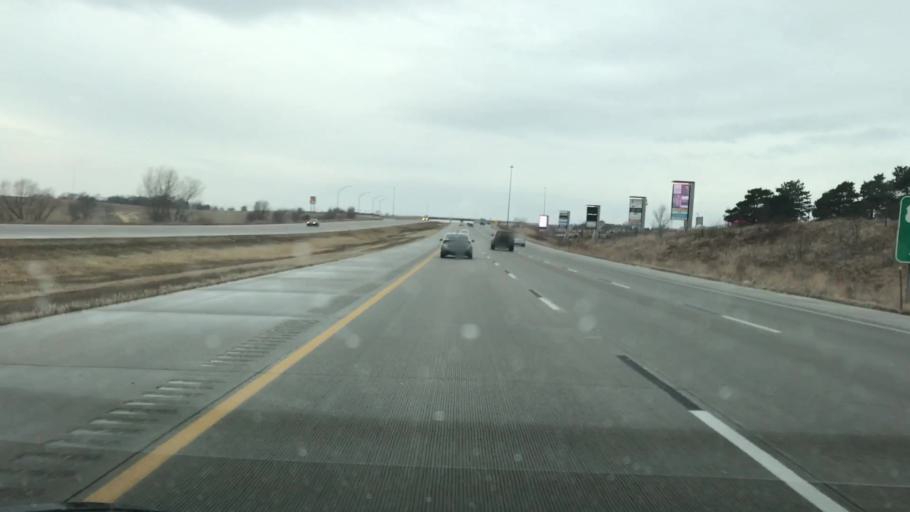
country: US
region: Nebraska
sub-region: Sarpy County
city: Gretna
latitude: 41.0994
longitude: -96.2440
